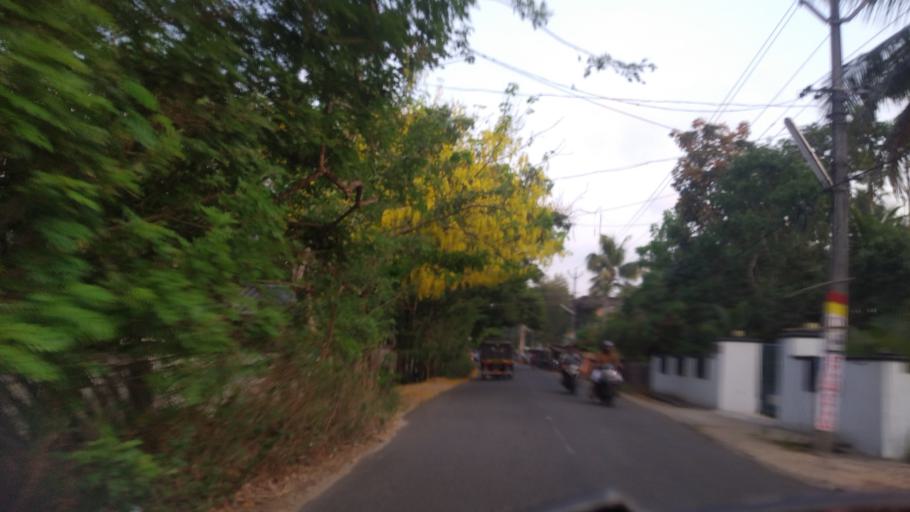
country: IN
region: Kerala
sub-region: Thrissur District
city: Kodungallur
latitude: 10.2441
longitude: 76.1499
